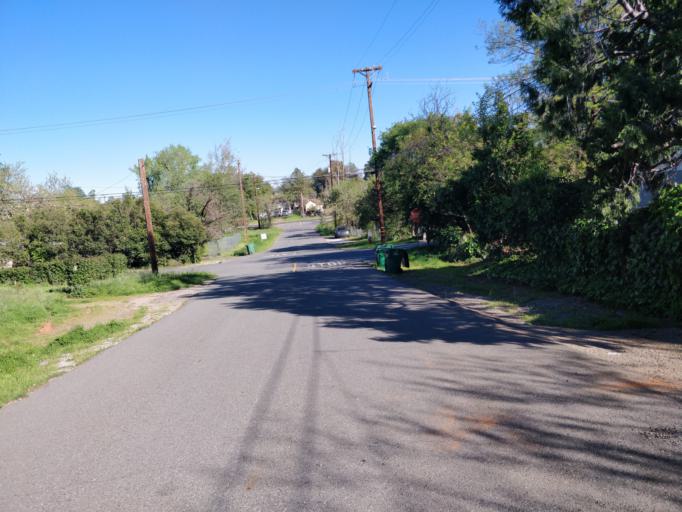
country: US
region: California
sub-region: Shasta County
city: Shasta Lake
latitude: 40.6779
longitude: -122.3545
